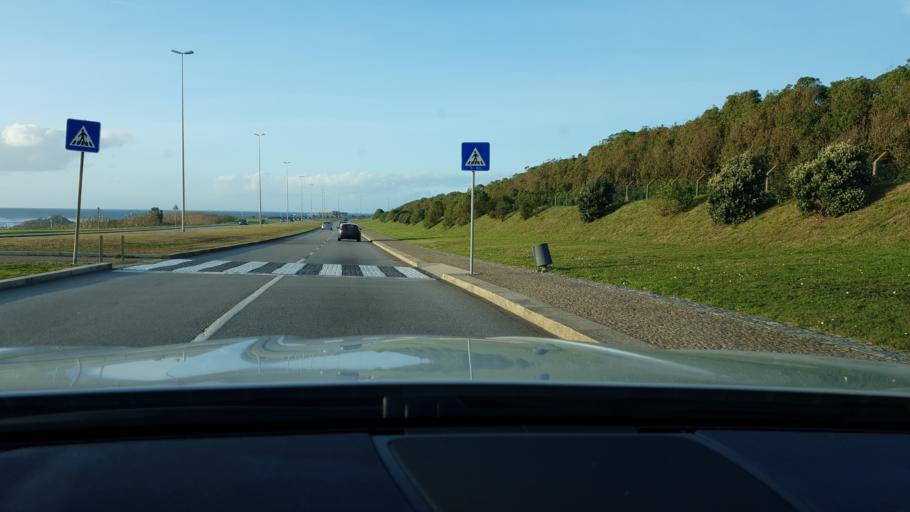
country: PT
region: Porto
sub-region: Matosinhos
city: Leca da Palmeira
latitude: 41.2028
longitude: -8.7121
